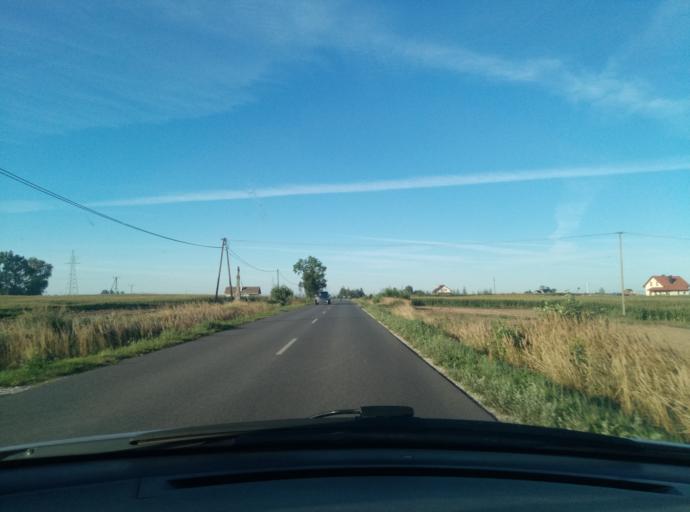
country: PL
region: Kujawsko-Pomorskie
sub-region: Powiat golubsko-dobrzynski
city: Kowalewo Pomorskie
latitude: 53.1859
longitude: 18.9071
